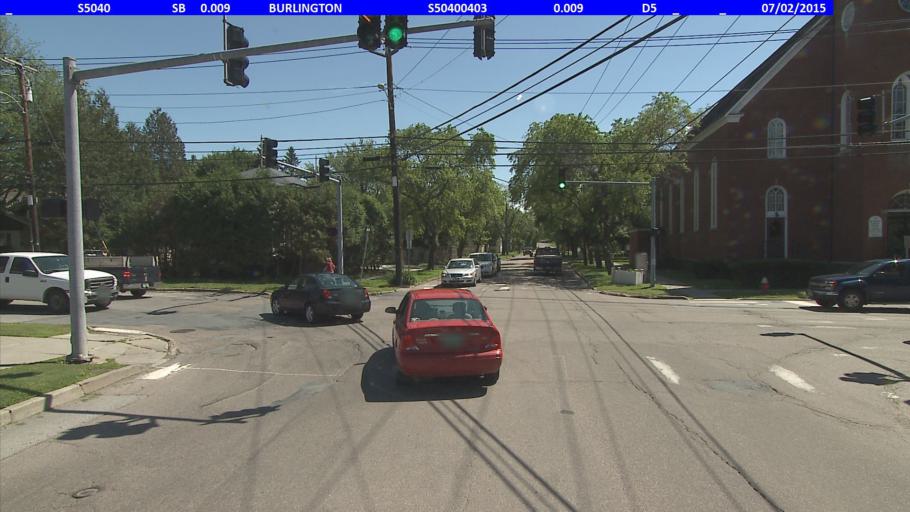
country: US
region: Vermont
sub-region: Chittenden County
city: Burlington
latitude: 44.4556
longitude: -73.2142
